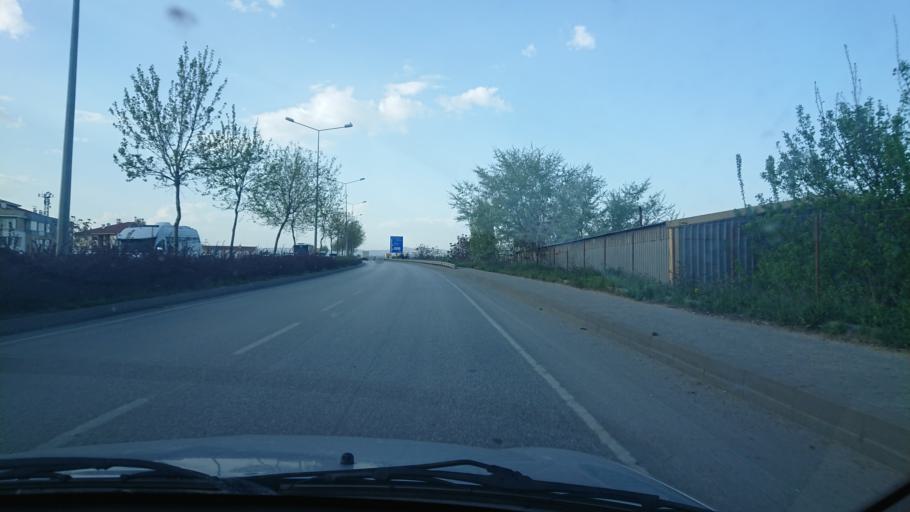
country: TR
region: Eskisehir
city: Eskisehir
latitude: 39.7721
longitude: 30.4835
